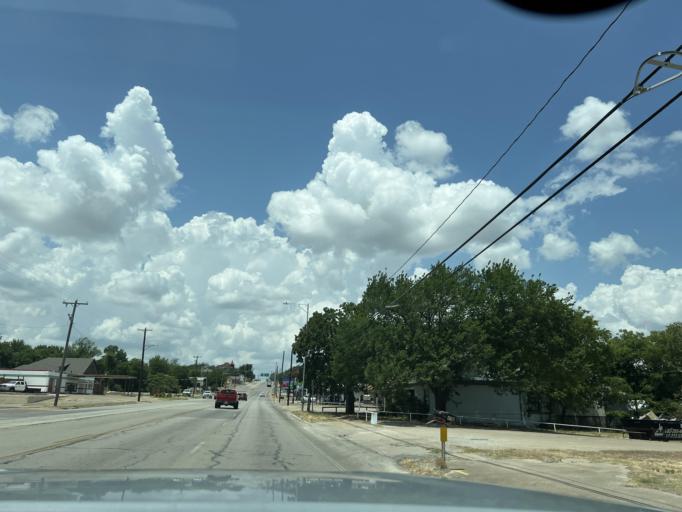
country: US
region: Texas
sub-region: Parker County
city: Weatherford
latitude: 32.7589
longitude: -97.8072
